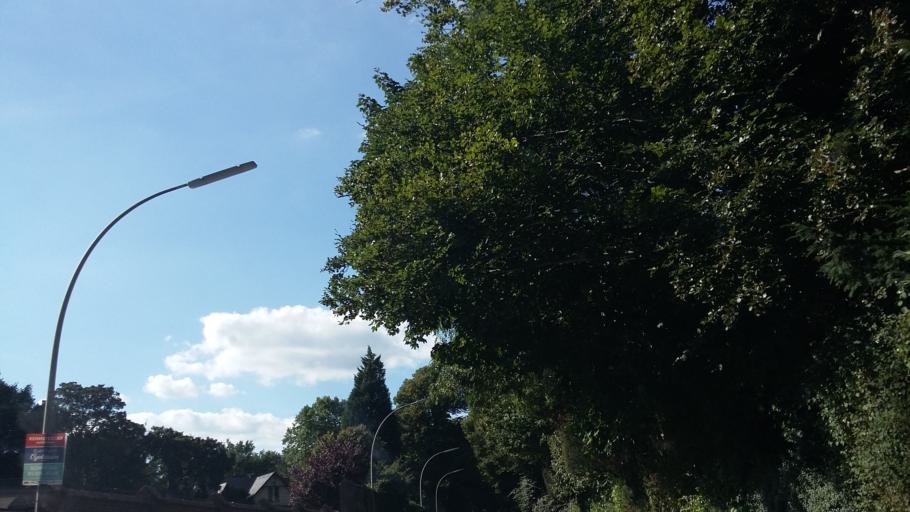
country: DE
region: Schleswig-Holstein
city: Halstenbek
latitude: 53.5518
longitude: 9.8412
